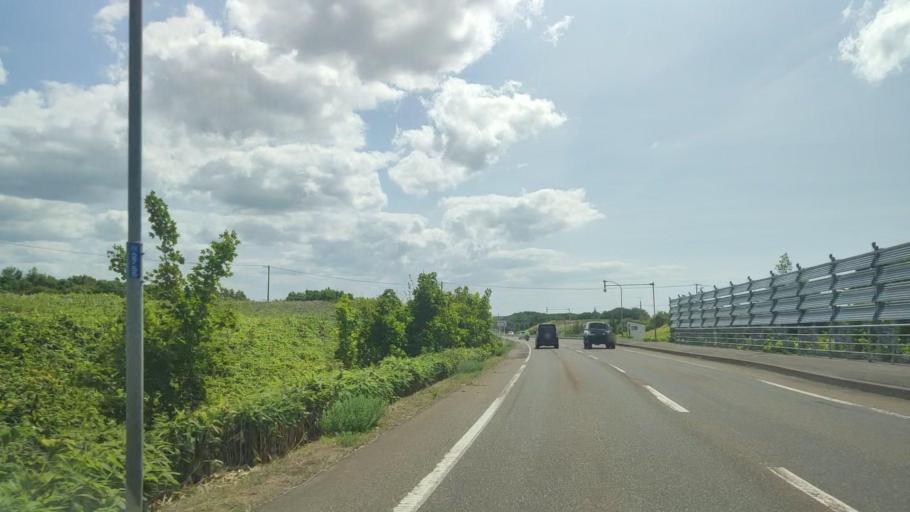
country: JP
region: Hokkaido
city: Makubetsu
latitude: 44.7865
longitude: 141.7901
